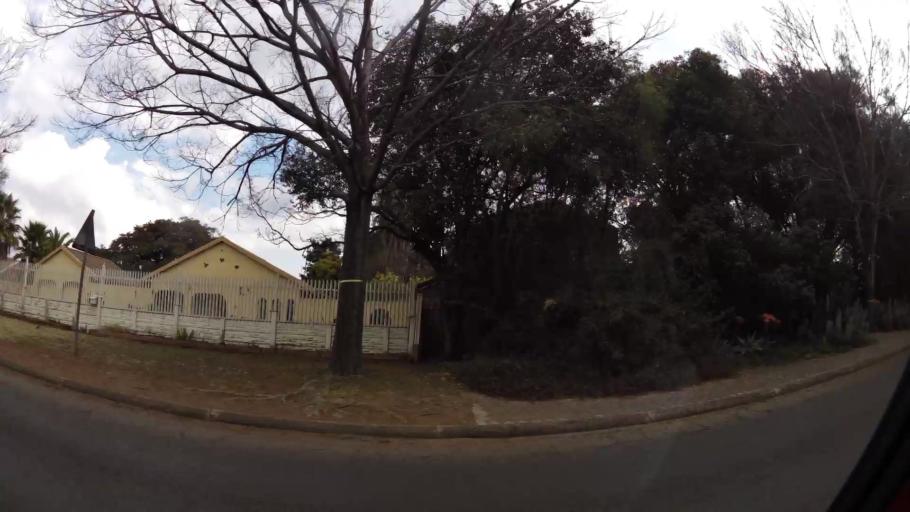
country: ZA
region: Gauteng
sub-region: Sedibeng District Municipality
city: Vanderbijlpark
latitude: -26.7175
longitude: 27.8236
